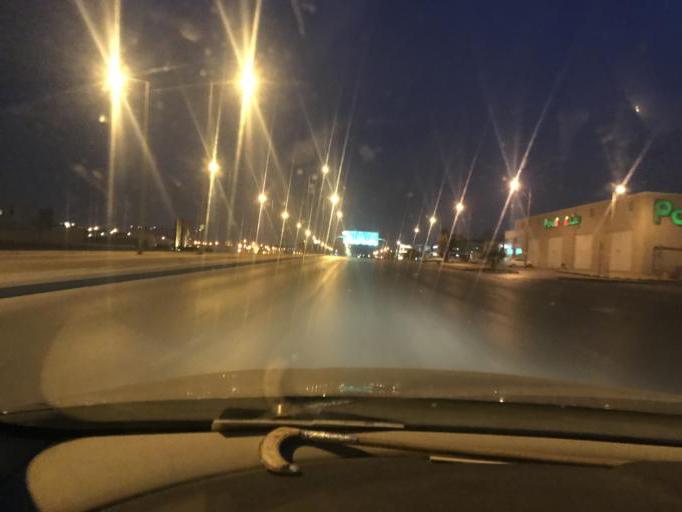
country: SA
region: Ar Riyad
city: Riyadh
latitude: 24.8079
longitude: 46.6927
